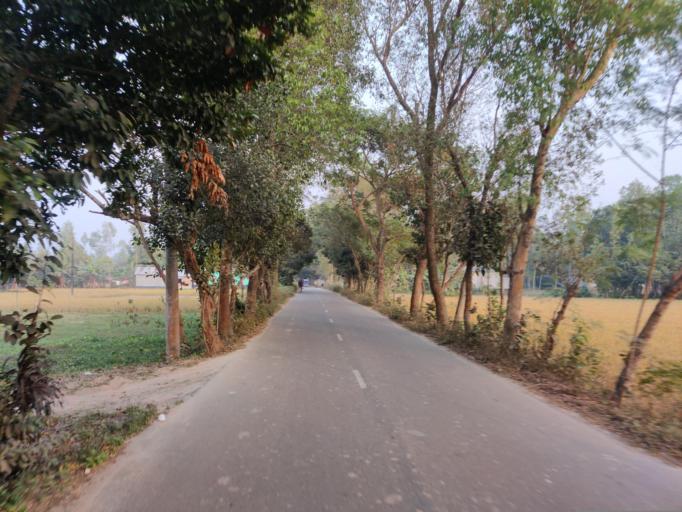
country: BD
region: Dhaka
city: Bajitpur
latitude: 24.1583
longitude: 90.8021
